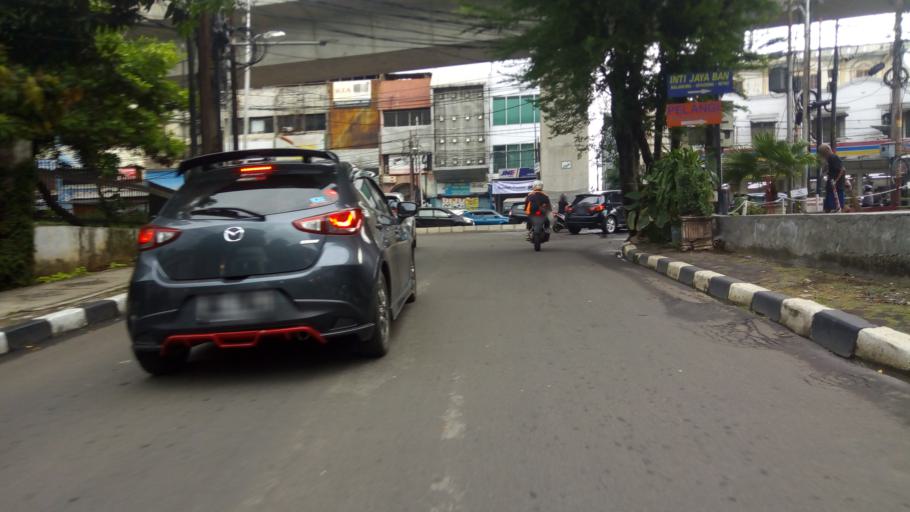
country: ID
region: Jakarta Raya
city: Jakarta
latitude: -6.2577
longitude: 106.7974
